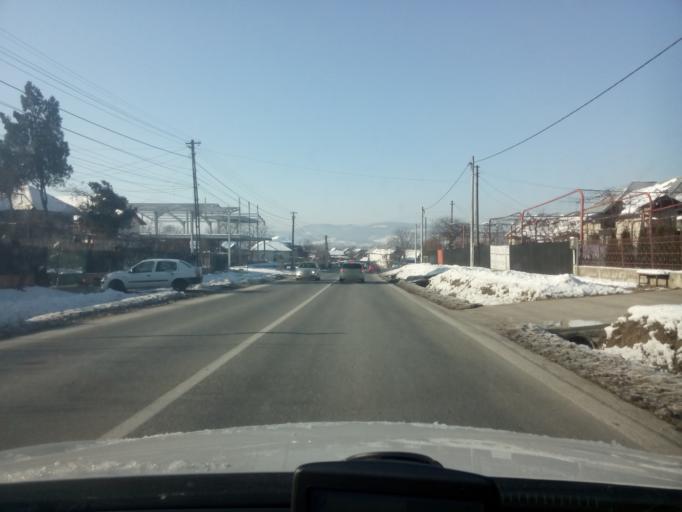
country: RO
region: Valcea
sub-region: Comuna Budesti
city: Budesti
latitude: 45.0757
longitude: 24.3927
